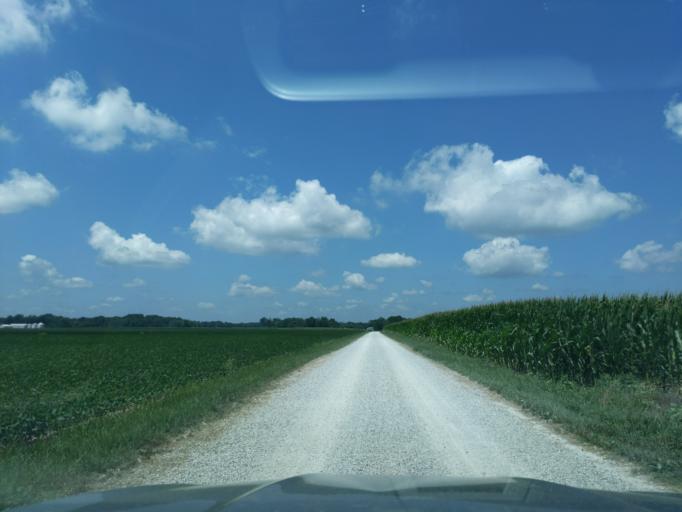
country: US
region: Indiana
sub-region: Ripley County
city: Osgood
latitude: 39.2203
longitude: -85.3811
